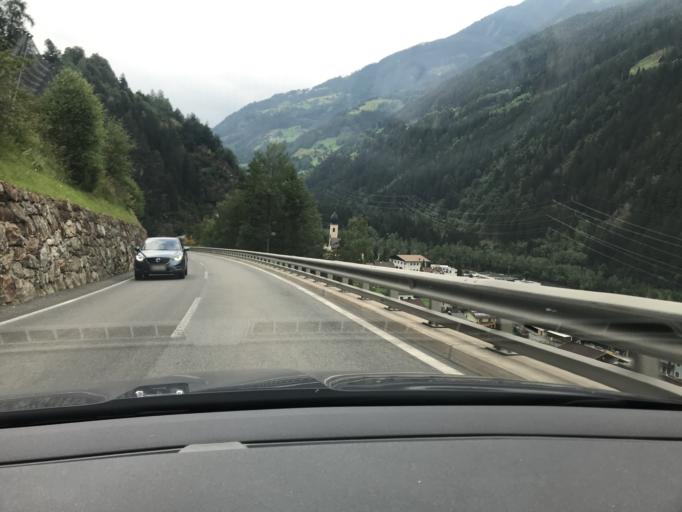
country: AT
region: Tyrol
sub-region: Politischer Bezirk Lienz
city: Hopfgarten in Defereggen
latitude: 46.9325
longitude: 12.5735
